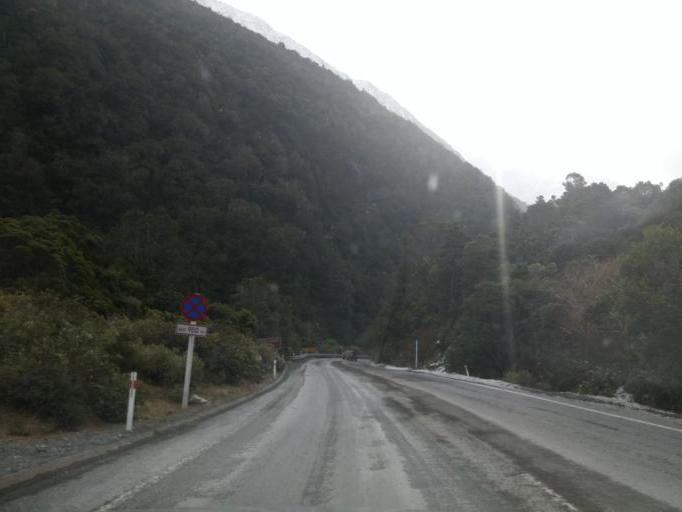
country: NZ
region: West Coast
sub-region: Grey District
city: Greymouth
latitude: -42.8830
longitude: 171.5556
